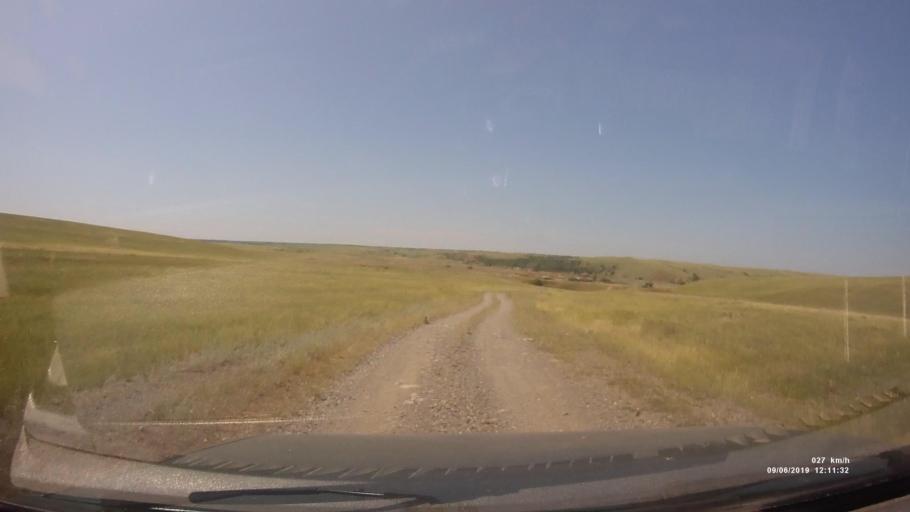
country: RU
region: Rostov
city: Staraya Stanitsa
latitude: 48.2502
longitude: 40.3344
